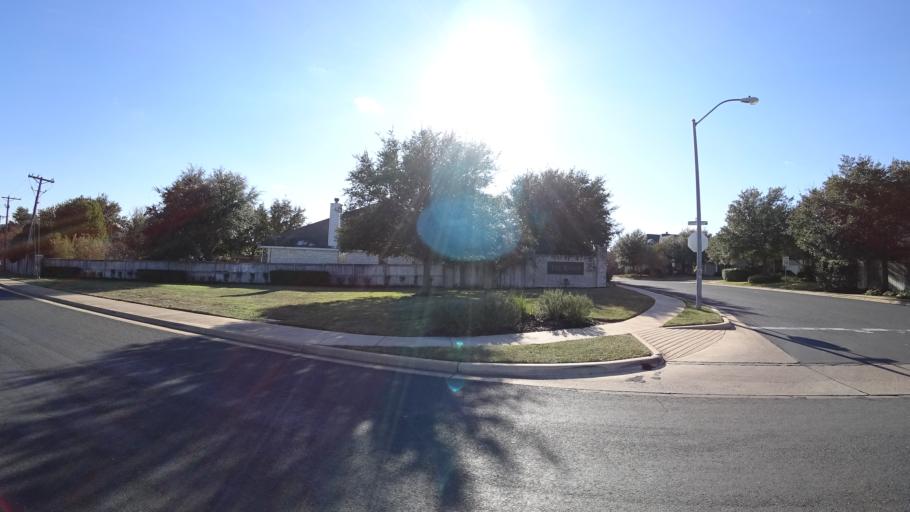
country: US
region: Texas
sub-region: Williamson County
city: Brushy Creek
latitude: 30.4903
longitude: -97.7328
